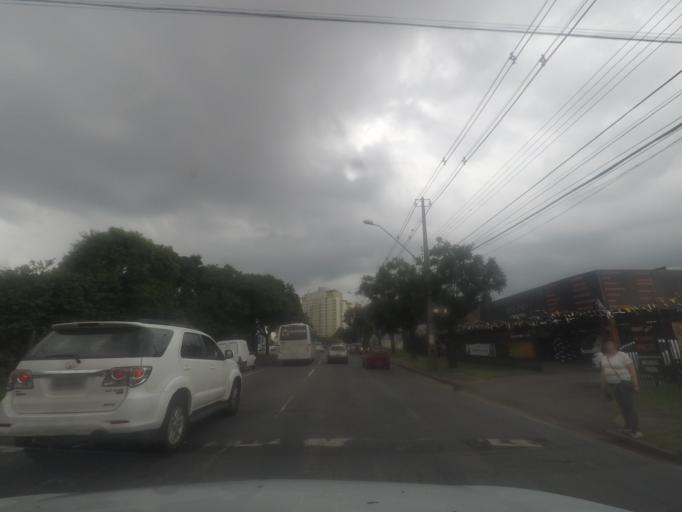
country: BR
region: Parana
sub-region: Curitiba
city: Curitiba
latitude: -25.4926
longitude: -49.2954
